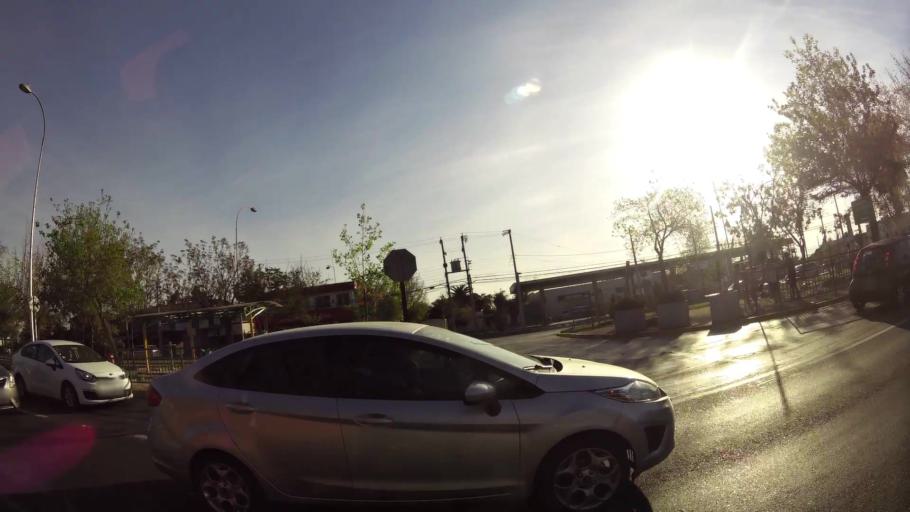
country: CL
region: Santiago Metropolitan
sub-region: Provincia de Cordillera
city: Puente Alto
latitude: -33.5362
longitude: -70.5730
